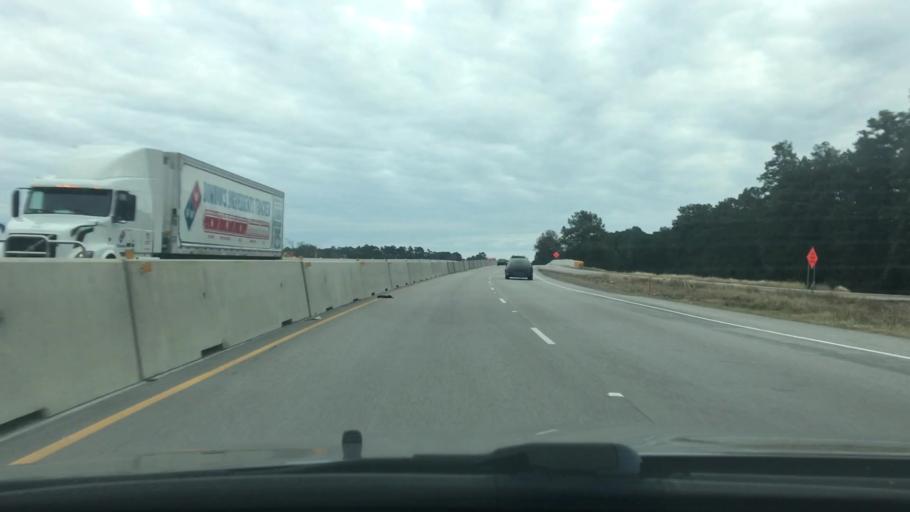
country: US
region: Texas
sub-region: Walker County
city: Huntsville
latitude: 30.6744
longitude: -95.5189
